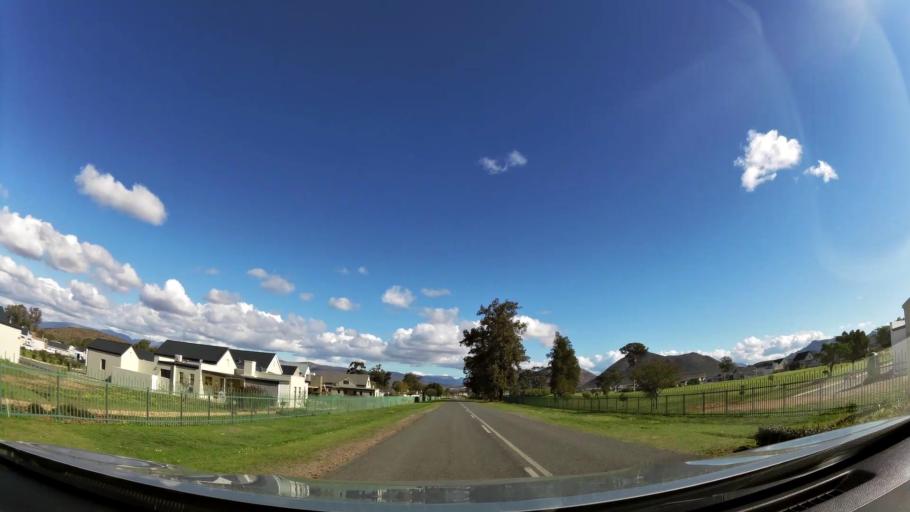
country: ZA
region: Western Cape
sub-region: Cape Winelands District Municipality
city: Ashton
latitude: -33.8087
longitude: 19.8569
